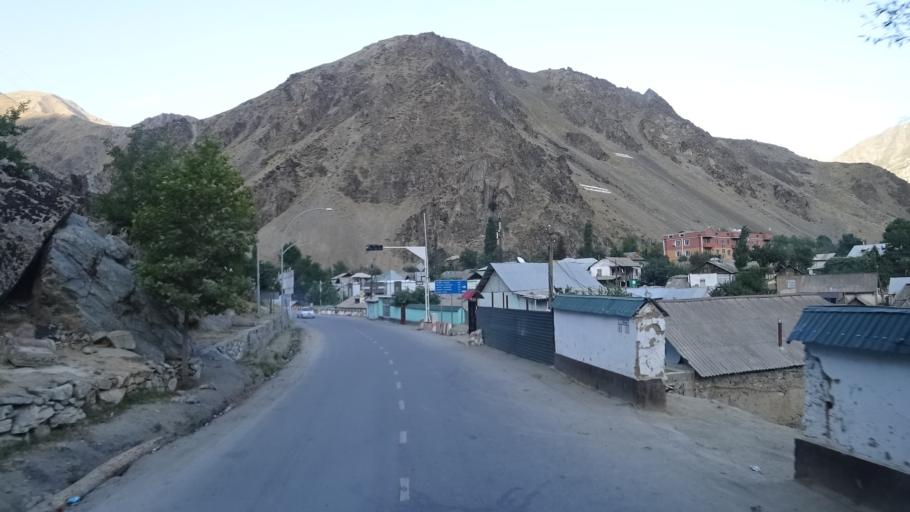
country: TJ
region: Gorno-Badakhshan
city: Qalaikhumb
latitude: 38.4568
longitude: 70.7871
